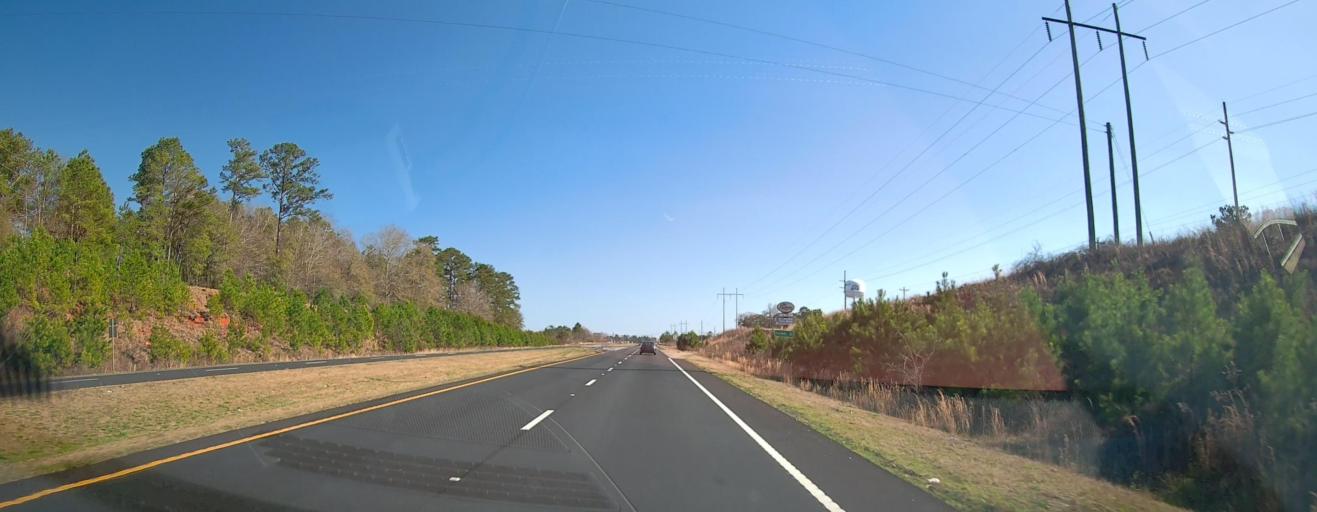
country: US
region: Georgia
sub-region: Sumter County
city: Americus
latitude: 32.0687
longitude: -84.2060
